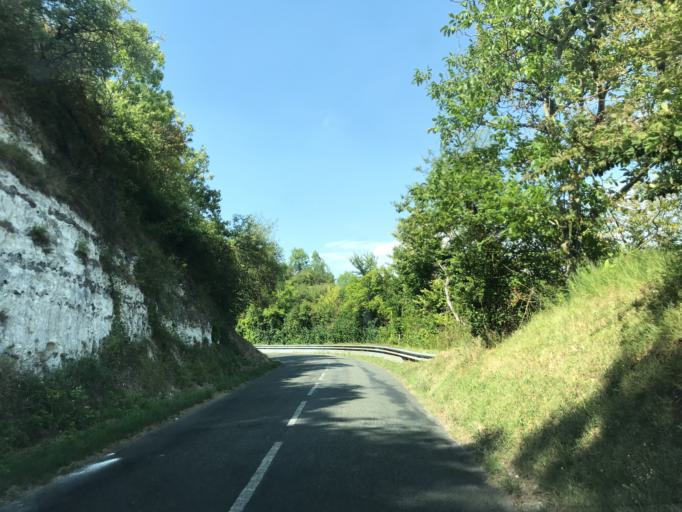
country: FR
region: Ile-de-France
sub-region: Departement des Yvelines
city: Freneuse
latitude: 49.0611
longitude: 1.5999
